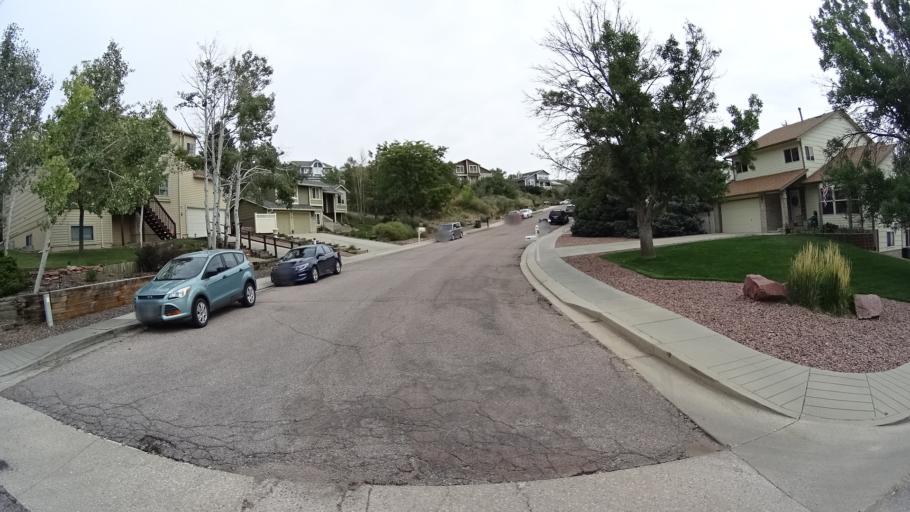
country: US
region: Colorado
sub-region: El Paso County
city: Cimarron Hills
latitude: 38.9075
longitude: -104.7263
